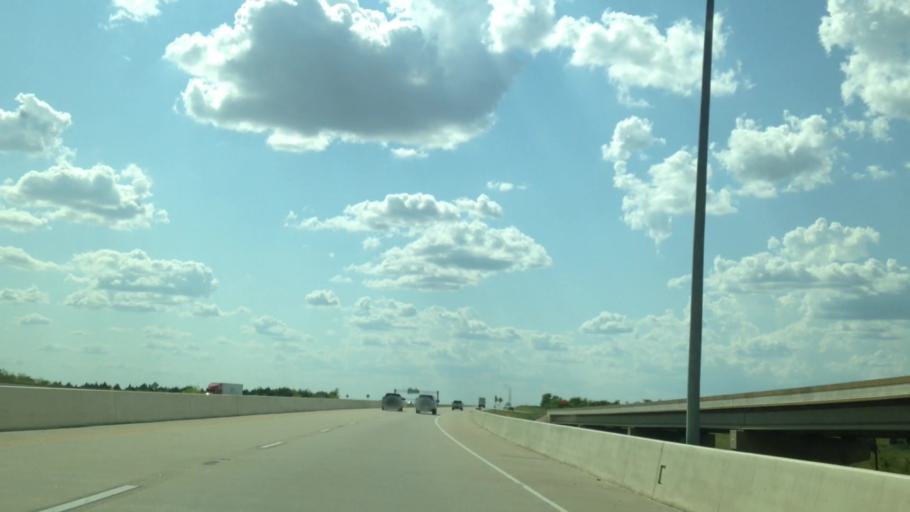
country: US
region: Texas
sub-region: Travis County
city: Onion Creek
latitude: 30.0809
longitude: -97.6998
